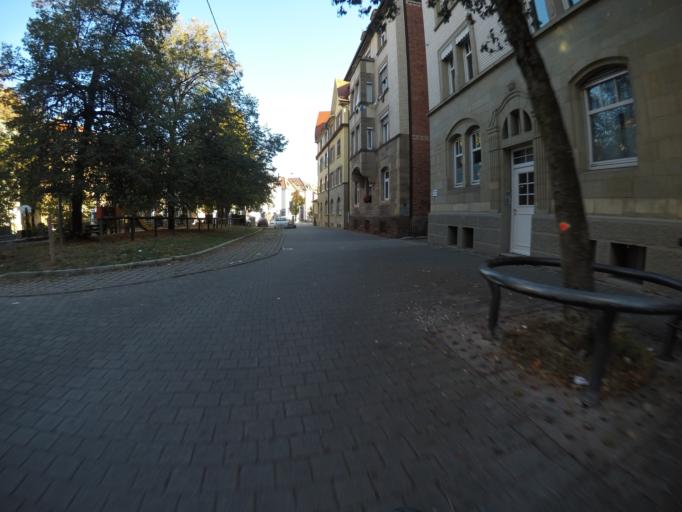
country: DE
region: Baden-Wuerttemberg
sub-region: Regierungsbezirk Stuttgart
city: Stuttgart
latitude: 48.7592
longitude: 9.1532
